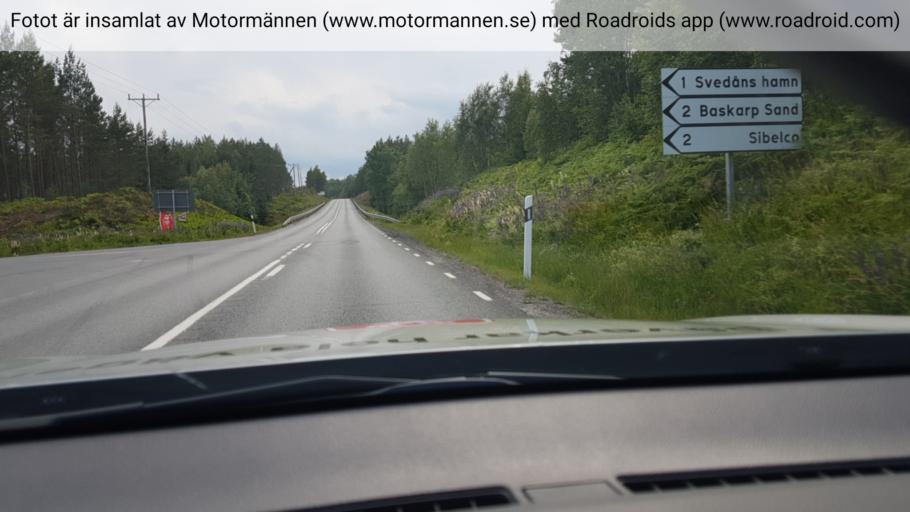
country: SE
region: Joenkoeping
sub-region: Habo Kommun
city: Habo
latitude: 58.0250
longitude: 14.1558
